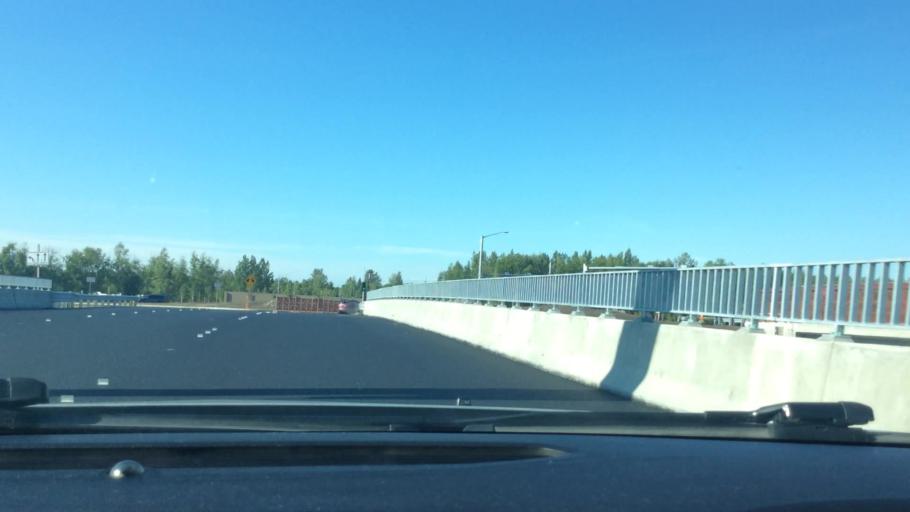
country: US
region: Alaska
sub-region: Anchorage Municipality
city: Elmendorf Air Force Base
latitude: 61.2269
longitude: -149.7340
